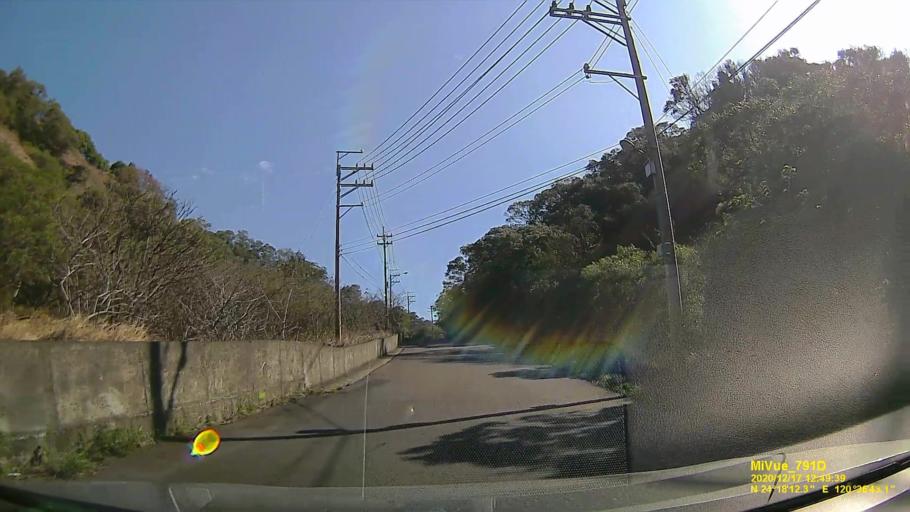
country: TW
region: Taiwan
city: Fengyuan
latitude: 24.3034
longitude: 120.6120
